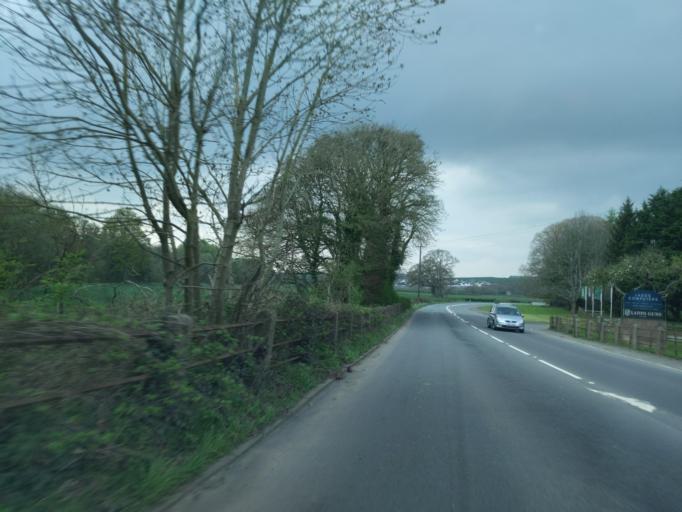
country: GB
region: England
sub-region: Devon
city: Crediton
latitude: 50.7804
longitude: -3.6243
